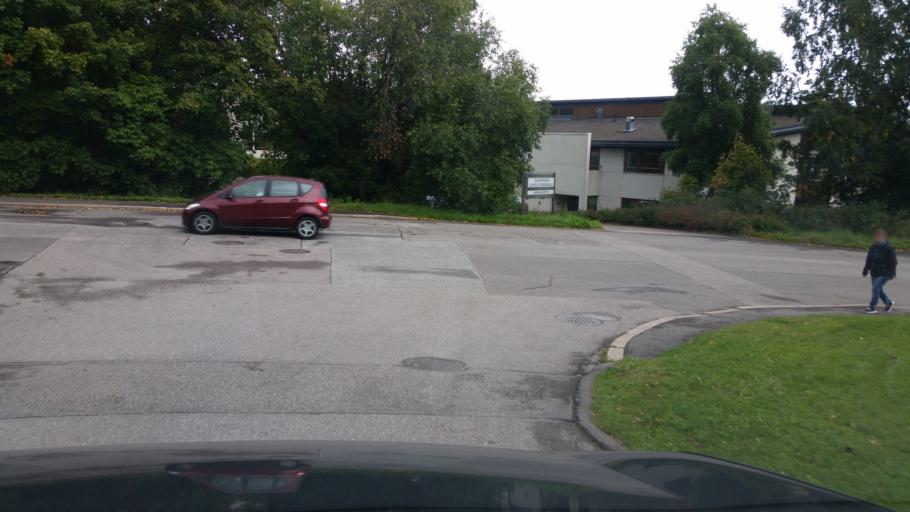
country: FI
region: Uusimaa
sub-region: Helsinki
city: Helsinki
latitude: 60.2370
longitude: 24.9707
